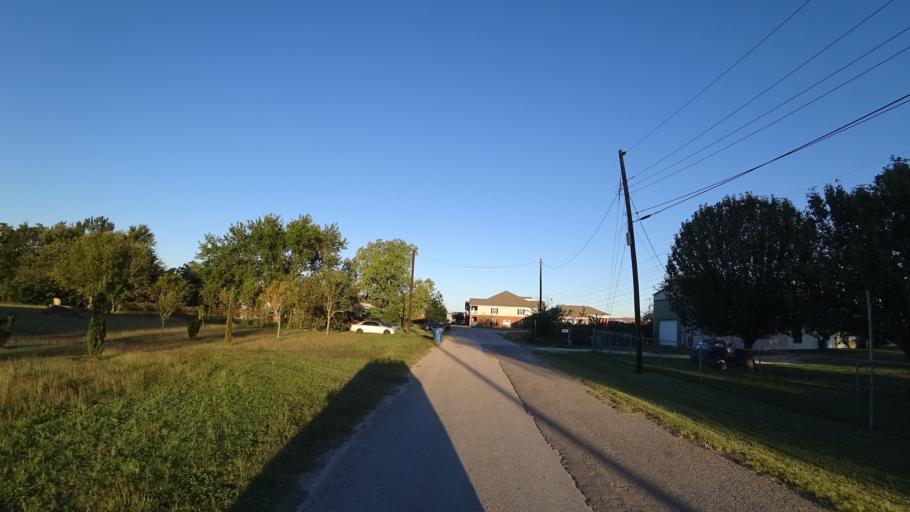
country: US
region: Texas
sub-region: Travis County
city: Hornsby Bend
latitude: 30.3079
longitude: -97.6203
